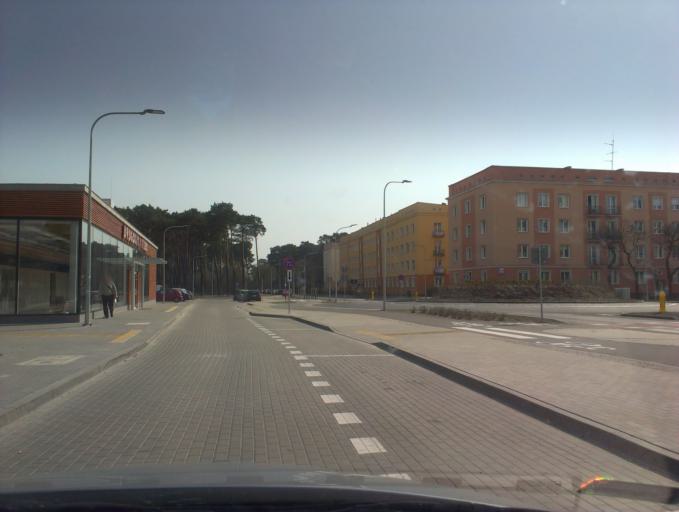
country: PL
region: Kujawsko-Pomorskie
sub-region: Bydgoszcz
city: Bydgoszcz
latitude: 53.1432
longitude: 18.0319
